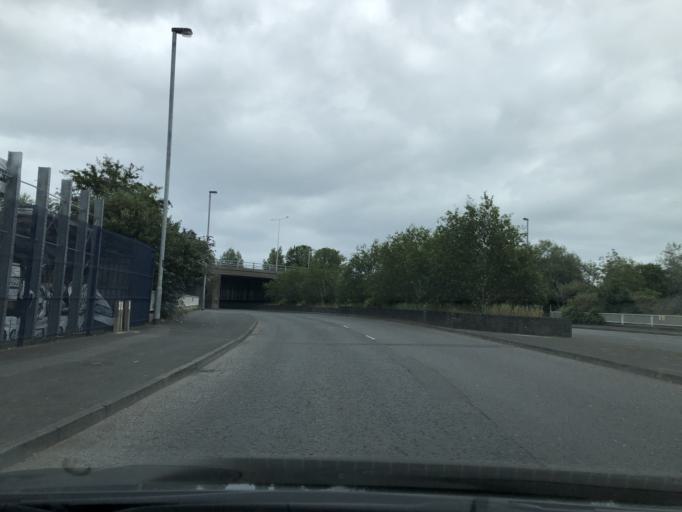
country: GB
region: Northern Ireland
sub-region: Larne District
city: Larne
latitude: 54.8487
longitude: -5.8198
